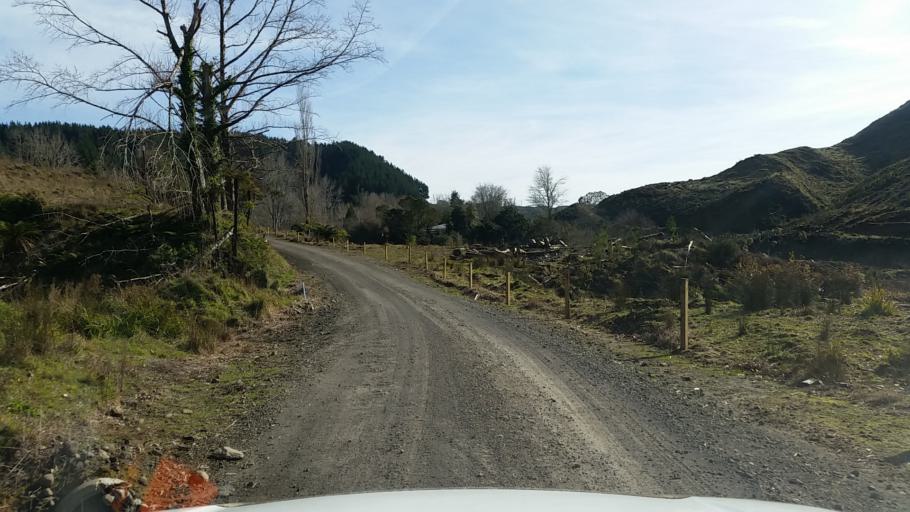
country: NZ
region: Taranaki
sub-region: South Taranaki District
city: Eltham
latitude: -39.3616
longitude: 174.5148
